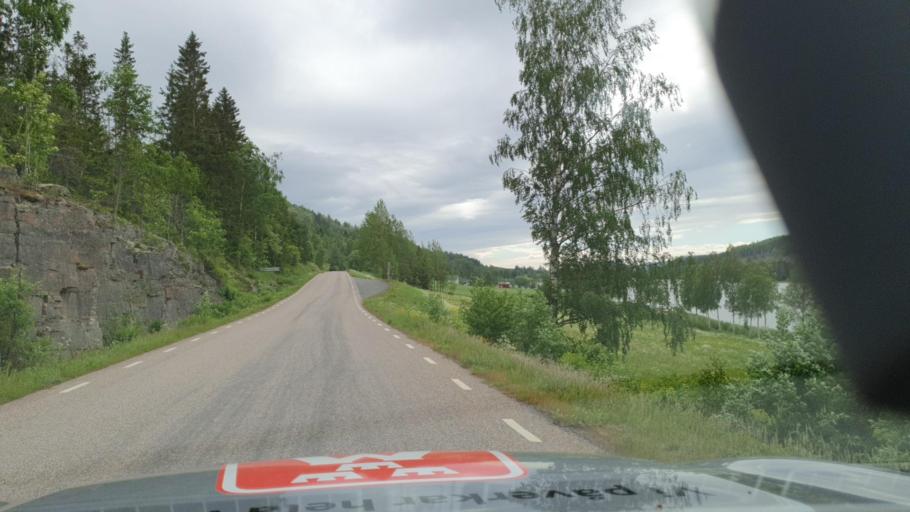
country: SE
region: Vaesternorrland
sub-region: Kramfors Kommun
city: Nordingra
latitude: 62.8802
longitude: 18.3393
